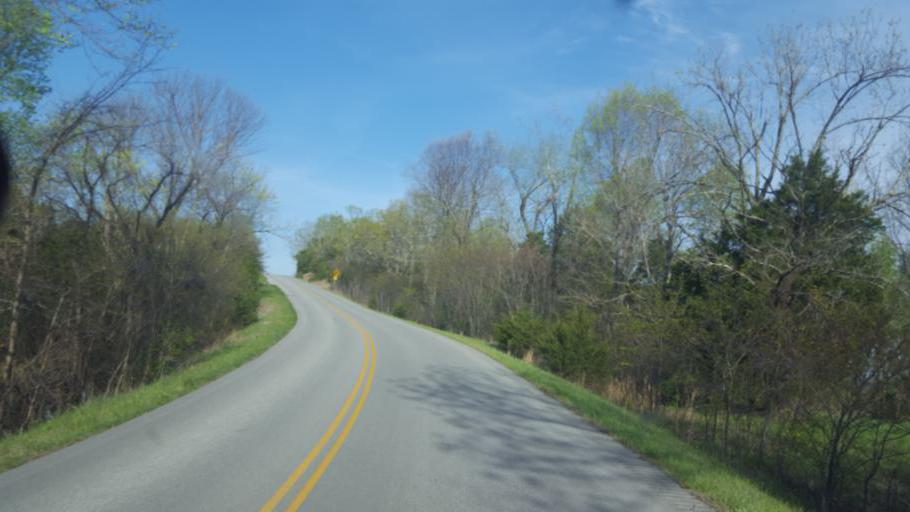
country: US
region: Kentucky
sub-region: Hart County
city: Munfordville
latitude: 37.3148
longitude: -86.0751
